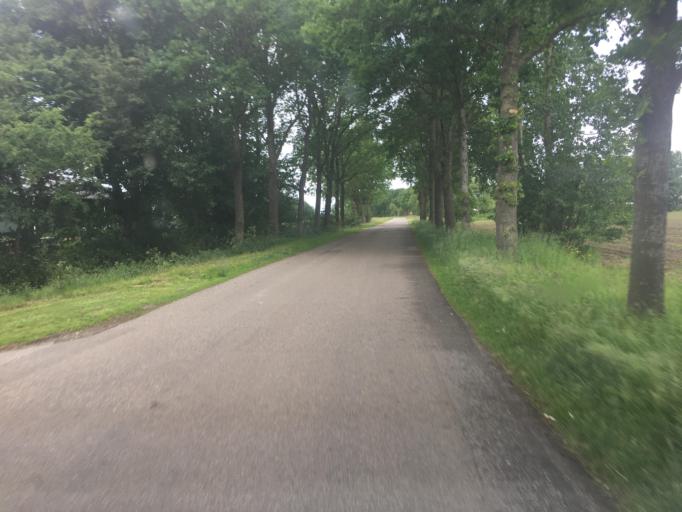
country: NL
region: Friesland
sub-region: Gemeente Skarsterlan
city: Oudehaske
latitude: 52.9005
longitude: 5.8894
